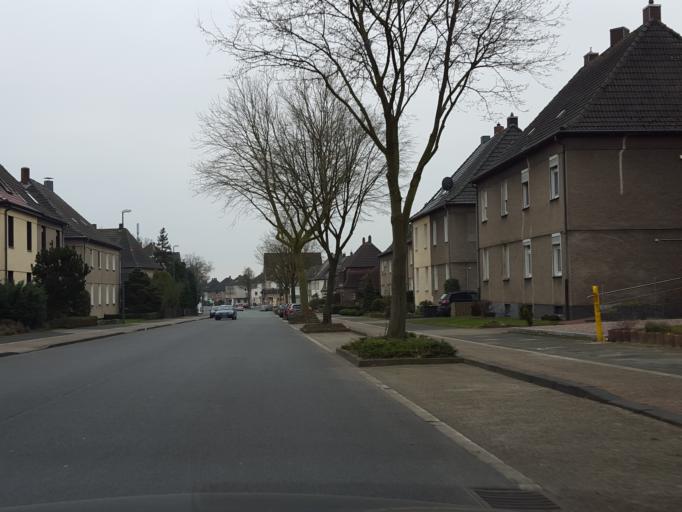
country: DE
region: North Rhine-Westphalia
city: Oer-Erkenschwick
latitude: 51.6514
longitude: 7.2534
